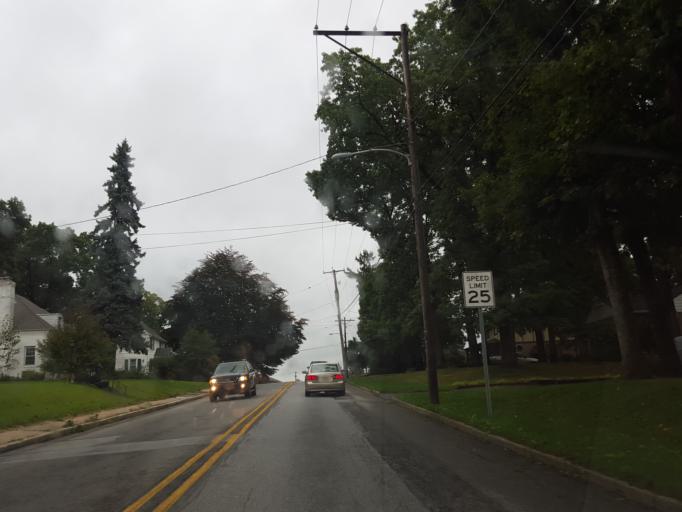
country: US
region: Pennsylvania
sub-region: York County
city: Red Lion
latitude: 39.9074
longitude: -76.6136
